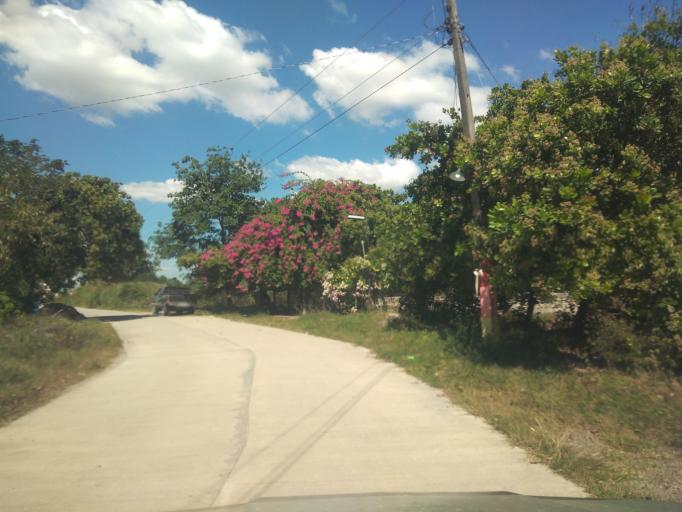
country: PH
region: Central Luzon
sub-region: Province of Pampanga
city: San Basilio
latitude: 15.0326
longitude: 120.6063
